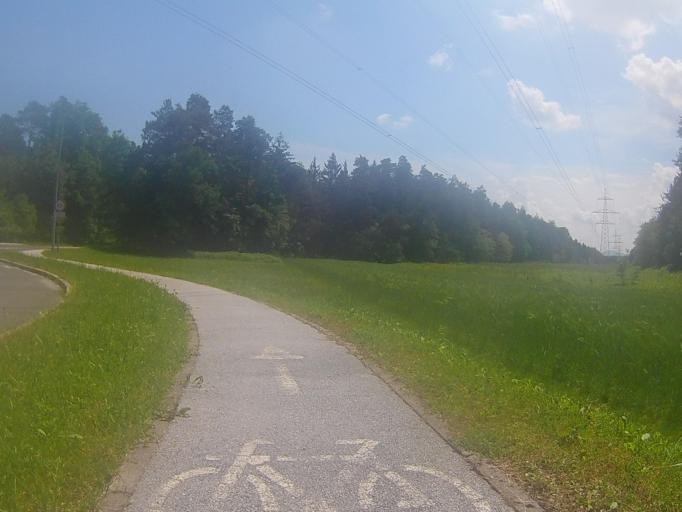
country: SI
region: Starse
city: Starse
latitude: 46.4386
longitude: 15.7737
